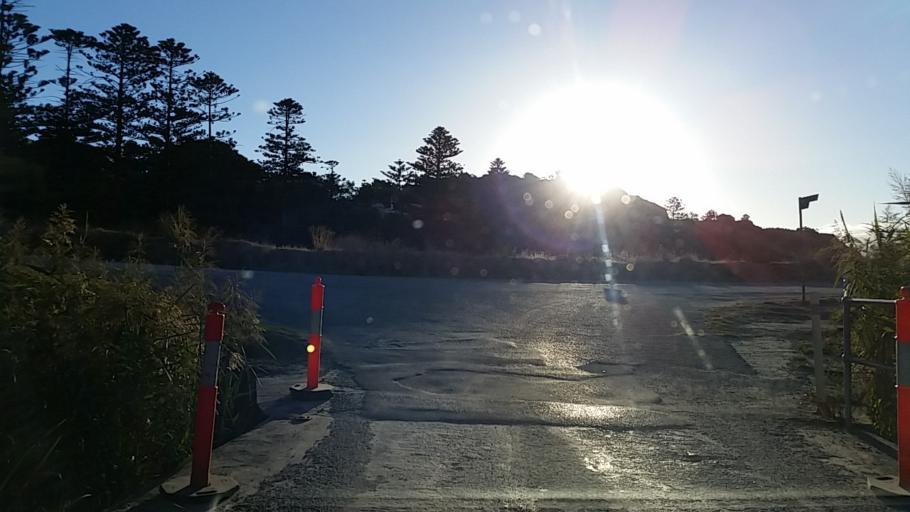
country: AU
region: South Australia
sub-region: Yankalilla
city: Normanville
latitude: -35.5255
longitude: 138.1902
